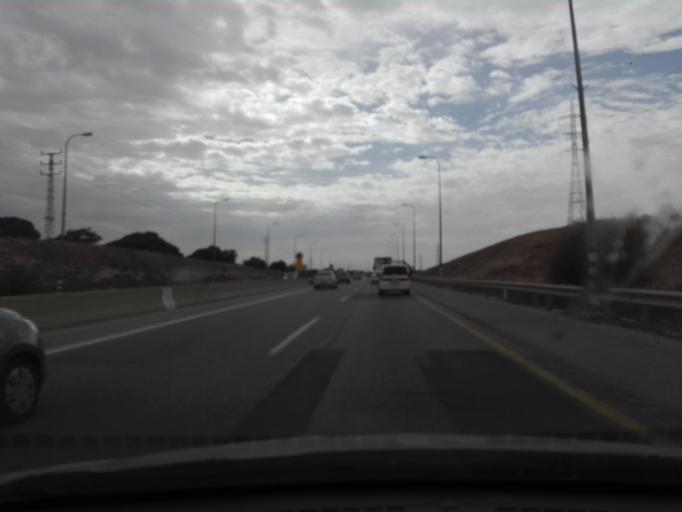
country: IL
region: Southern District
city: Lehavim
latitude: 31.3413
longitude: 34.7894
